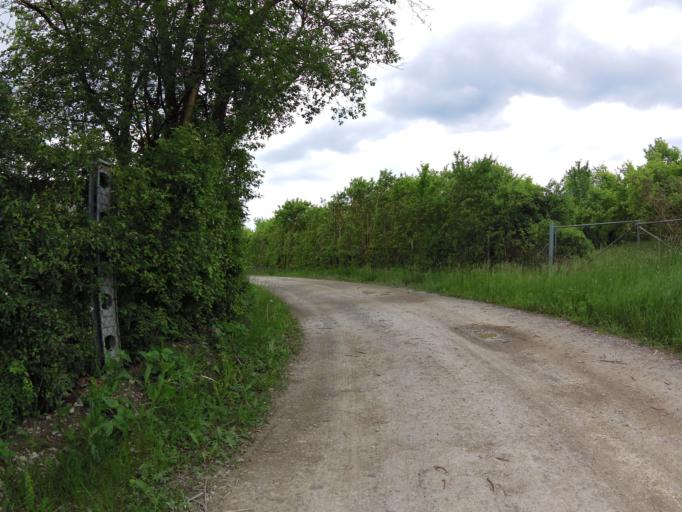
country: DE
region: Bavaria
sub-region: Regierungsbezirk Unterfranken
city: Winterhausen
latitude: 49.7251
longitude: 10.0270
